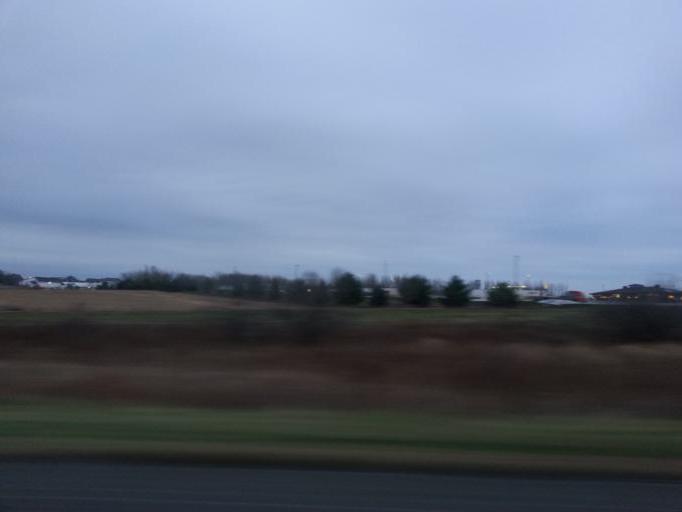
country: US
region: Iowa
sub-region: Linn County
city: Center Point
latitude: 42.1720
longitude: -91.7811
